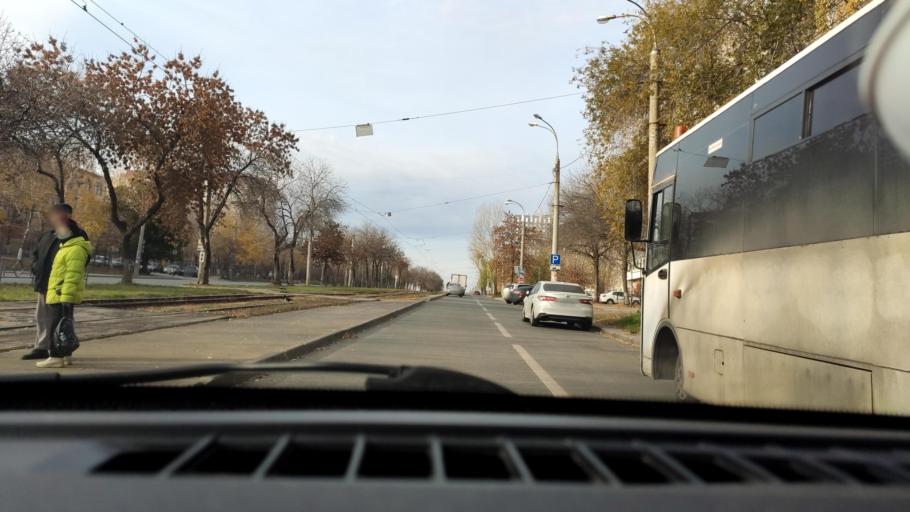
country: RU
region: Samara
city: Samara
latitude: 53.2125
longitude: 50.2097
